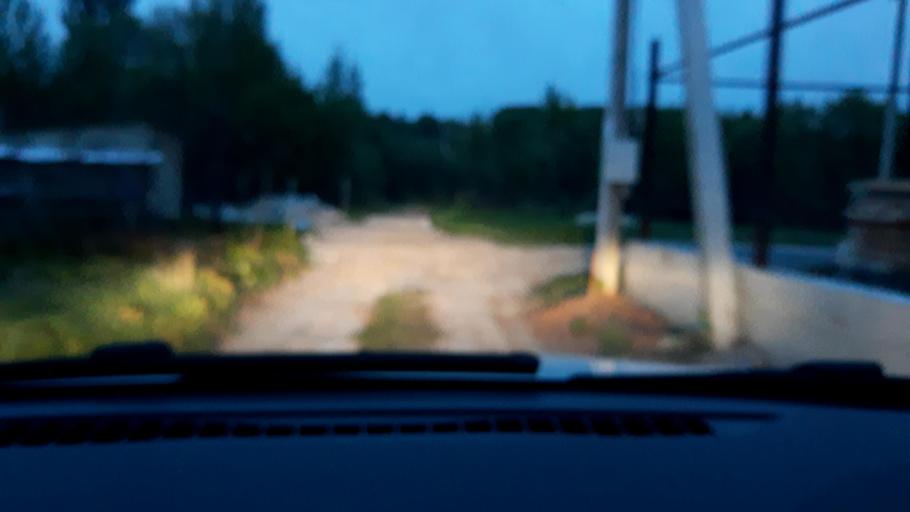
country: RU
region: Nizjnij Novgorod
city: Afonino
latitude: 56.2586
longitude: 44.0782
